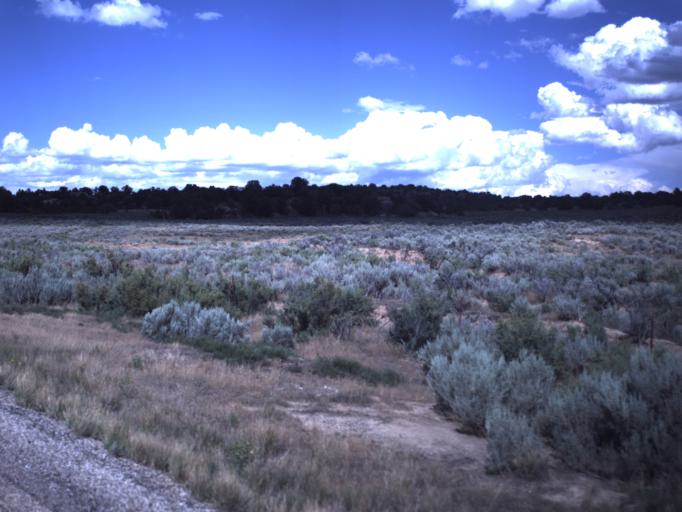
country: US
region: Utah
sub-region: Duchesne County
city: Duchesne
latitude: 40.2412
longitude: -110.7147
